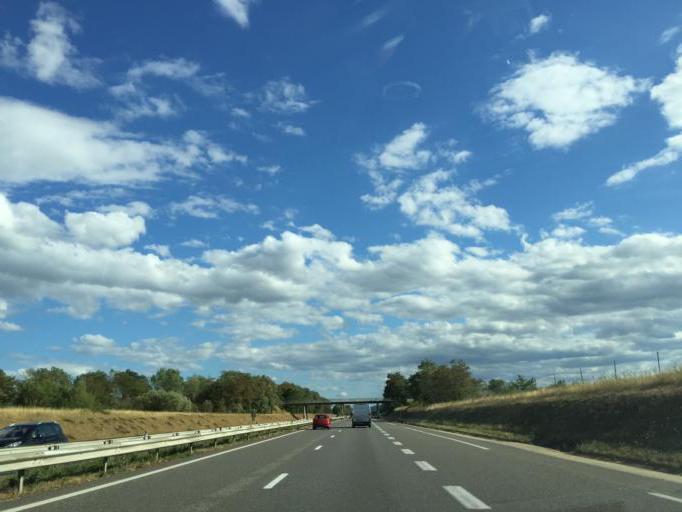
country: FR
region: Rhone-Alpes
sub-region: Departement de la Loire
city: Cuzieu
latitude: 45.6009
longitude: 4.2096
